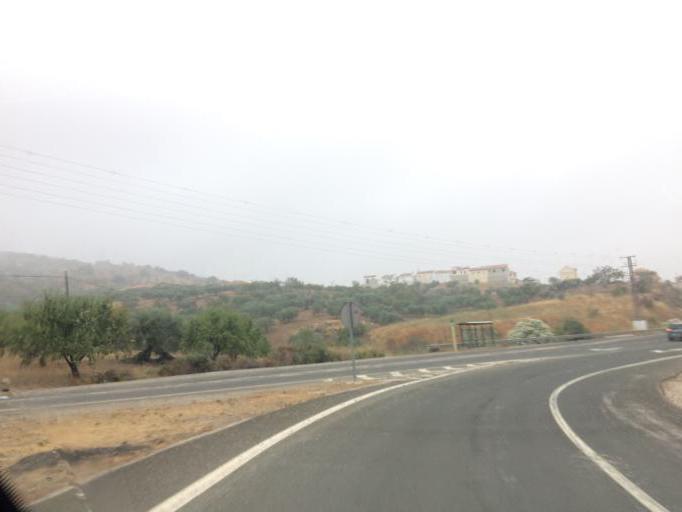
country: ES
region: Andalusia
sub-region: Provincia de Malaga
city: Casabermeja
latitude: 36.9015
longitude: -4.4414
